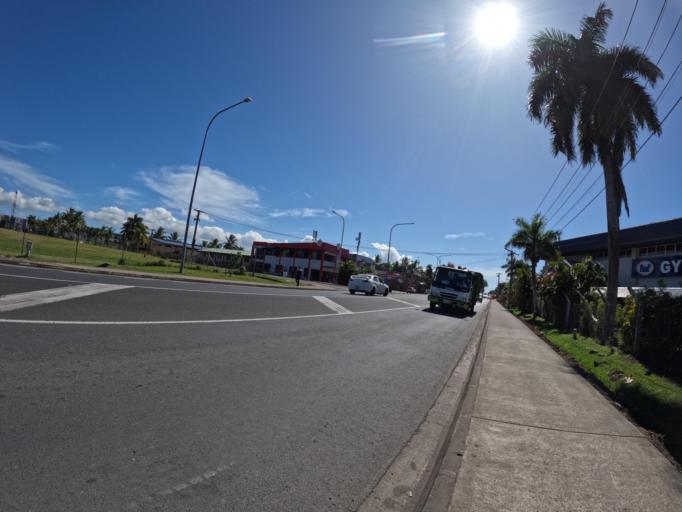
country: FJ
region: Central
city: Suva
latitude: -18.1485
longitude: 178.4502
